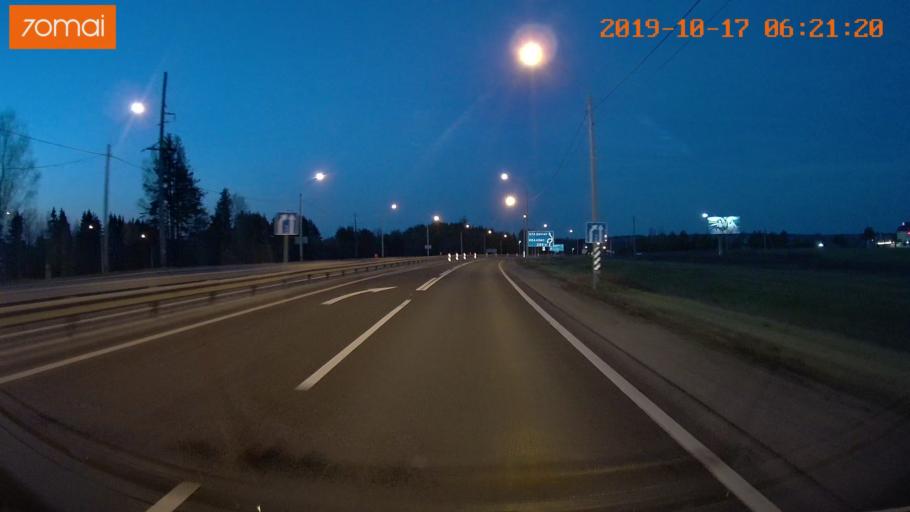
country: RU
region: Ivanovo
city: Lezhnevo
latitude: 56.8035
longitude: 40.8862
